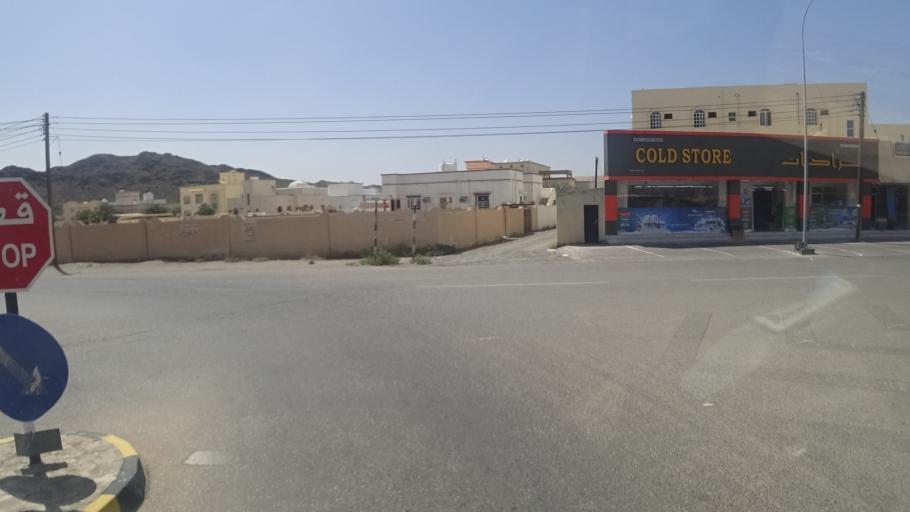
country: OM
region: Ash Sharqiyah
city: Ibra'
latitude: 22.6756
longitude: 58.5299
